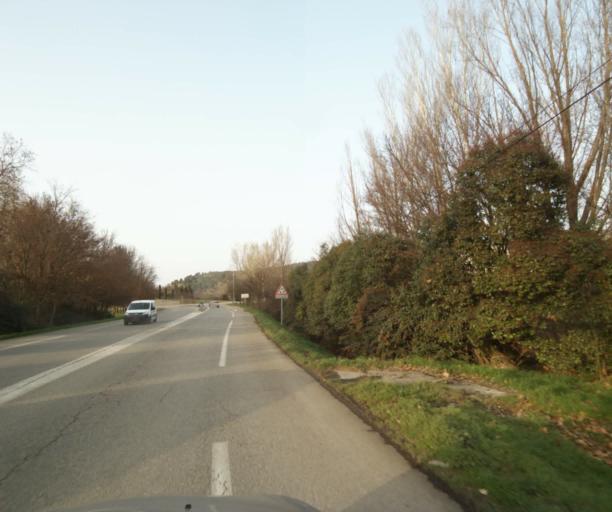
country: FR
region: Provence-Alpes-Cote d'Azur
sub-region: Departement des Bouches-du-Rhone
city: Rognes
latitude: 43.6564
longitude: 5.3556
